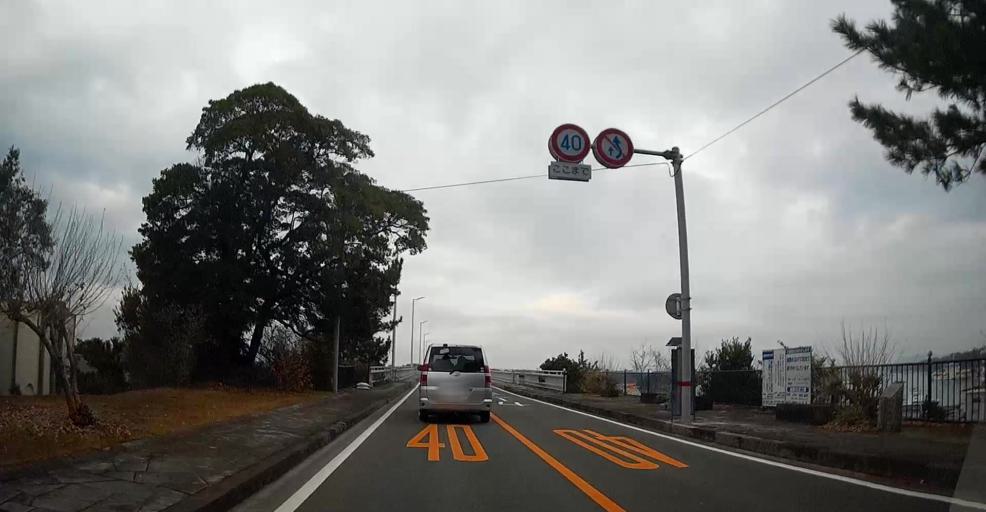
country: JP
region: Kumamoto
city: Yatsushiro
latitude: 32.5270
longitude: 130.4248
